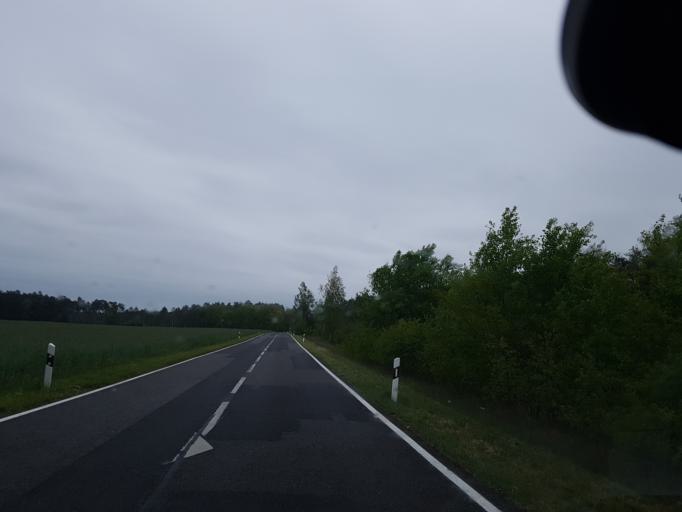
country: DE
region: Brandenburg
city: Drebkau
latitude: 51.6540
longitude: 14.2831
